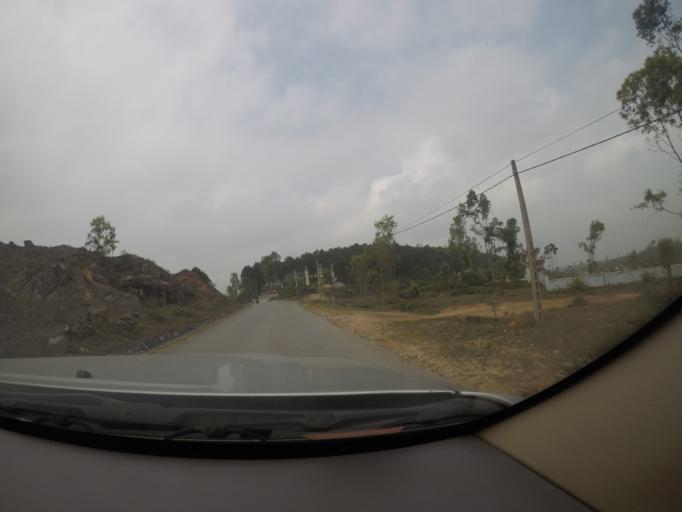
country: VN
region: Quang Binh
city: Ba Don
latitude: 17.6880
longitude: 106.4290
